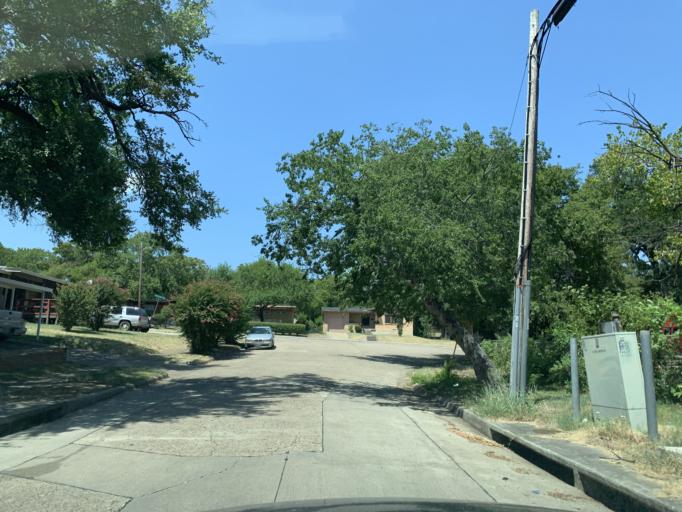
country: US
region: Texas
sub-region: Dallas County
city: Cockrell Hill
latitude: 32.6918
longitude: -96.8074
